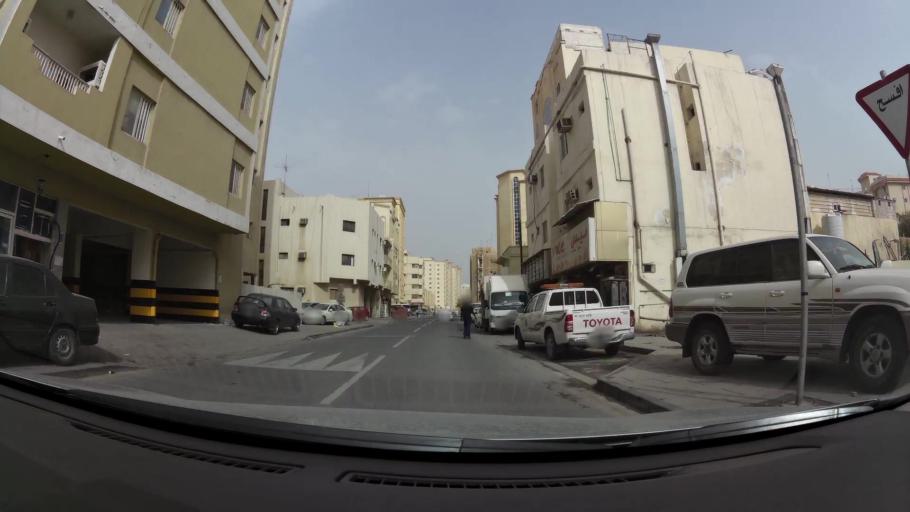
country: QA
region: Baladiyat ad Dawhah
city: Doha
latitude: 25.2750
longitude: 51.5458
